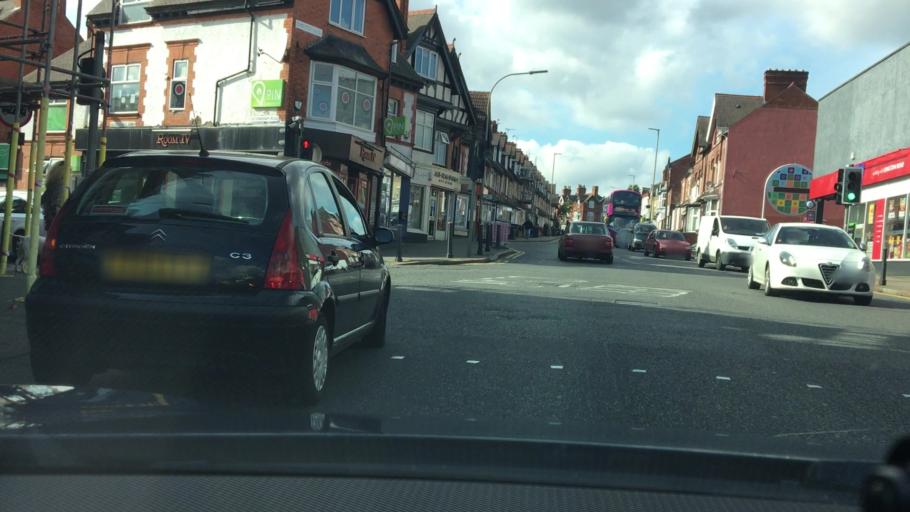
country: GB
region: England
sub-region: City of Leicester
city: Leicester
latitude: 52.6261
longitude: -1.1108
